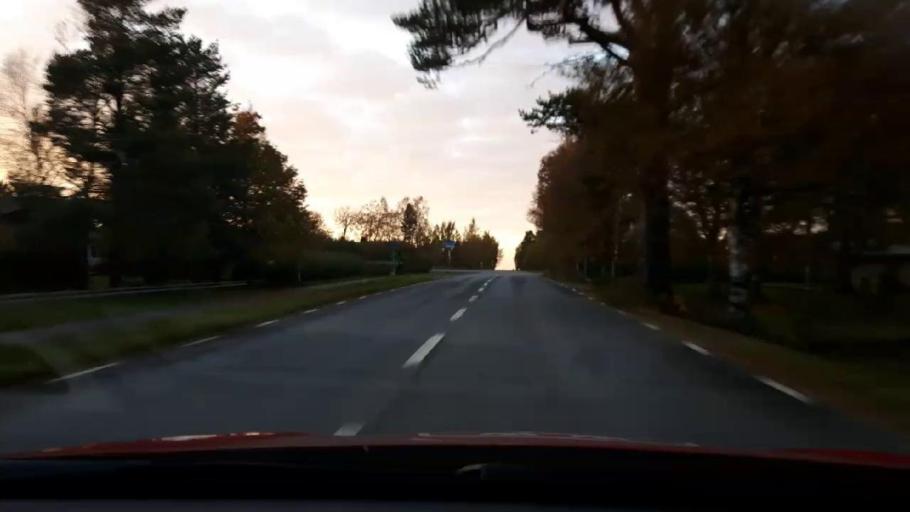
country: SE
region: Jaemtland
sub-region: OEstersunds Kommun
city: Ostersund
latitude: 63.2466
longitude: 14.5711
